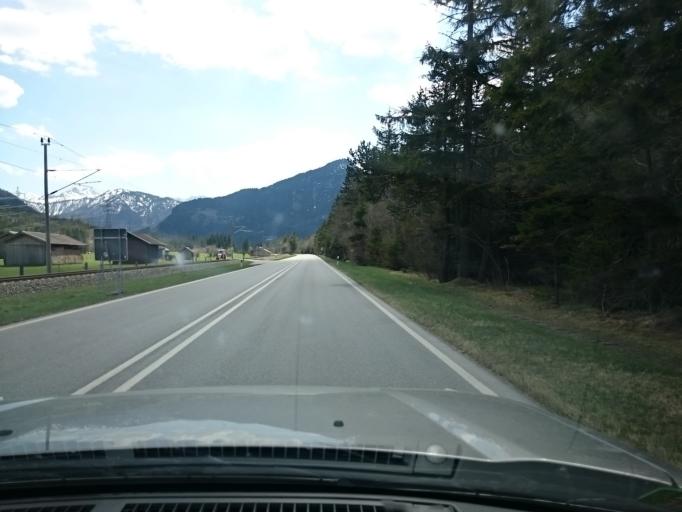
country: DE
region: Bavaria
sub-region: Upper Bavaria
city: Mittenwald
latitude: 47.4220
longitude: 11.2588
